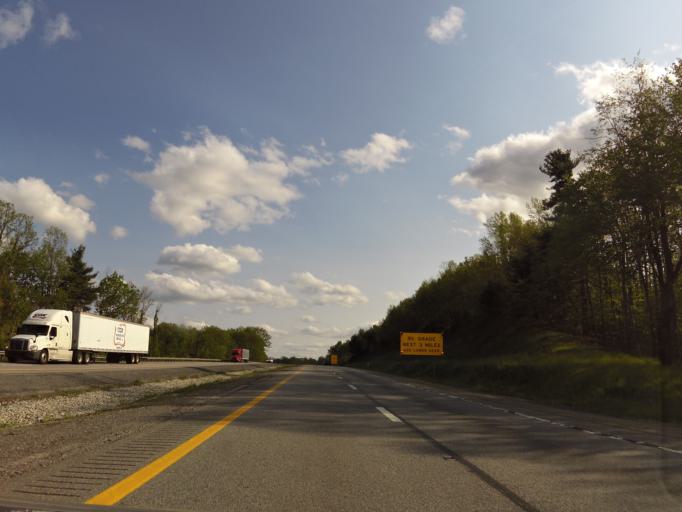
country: US
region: West Virginia
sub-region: Mercer County
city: Athens
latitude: 37.5471
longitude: -81.1152
